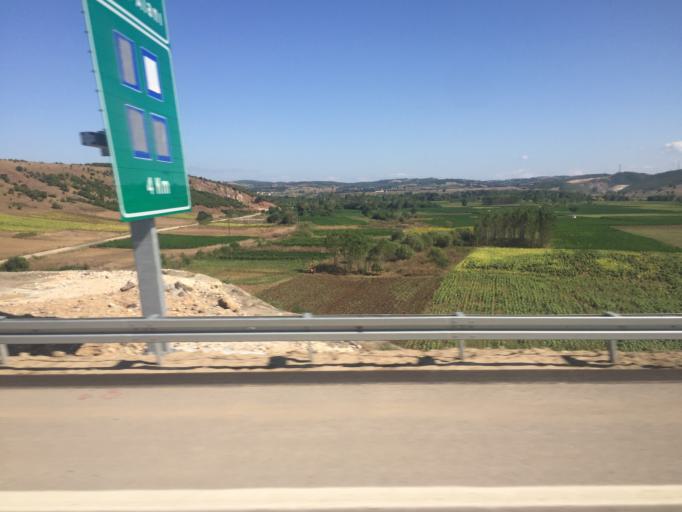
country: TR
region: Bursa
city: Mahmudiye
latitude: 40.2651
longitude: 28.6541
